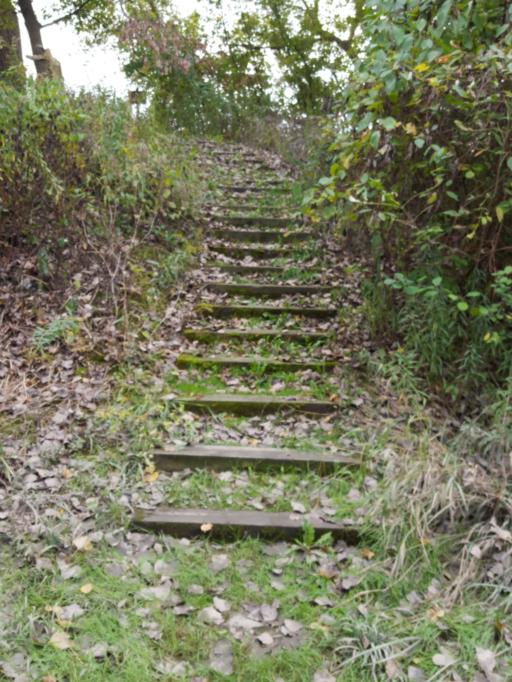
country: US
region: Illinois
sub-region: Cook County
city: Northfield
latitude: 42.0946
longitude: -87.8102
